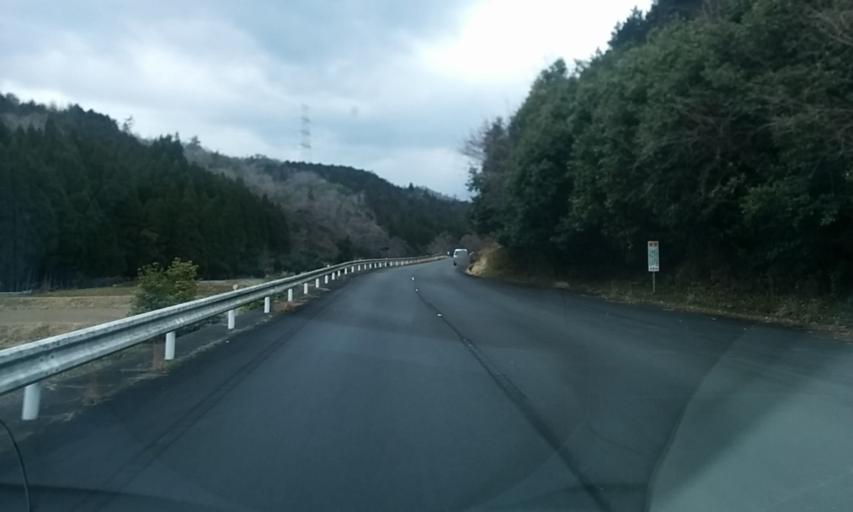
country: JP
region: Kyoto
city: Kameoka
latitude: 35.1093
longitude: 135.4396
